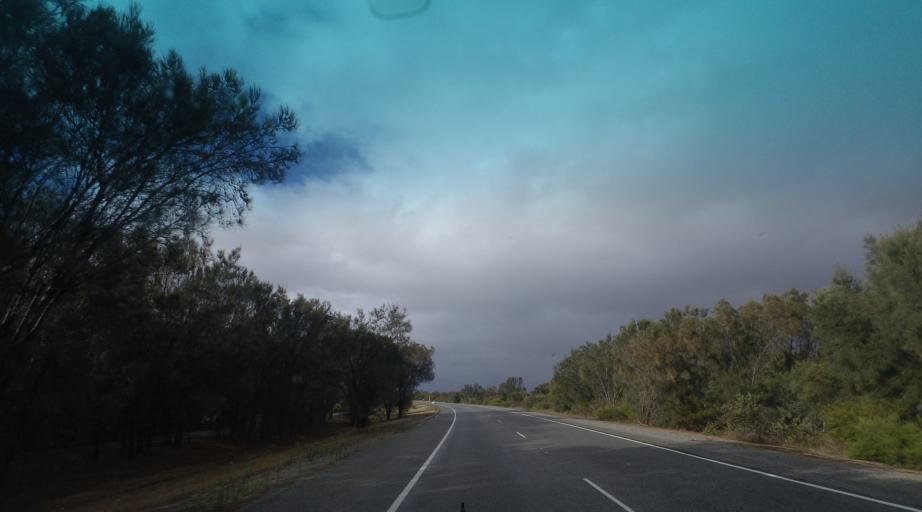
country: AU
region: Western Australia
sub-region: Serpentine-Jarrahdale
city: Oakford
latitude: -32.1963
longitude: 115.9625
